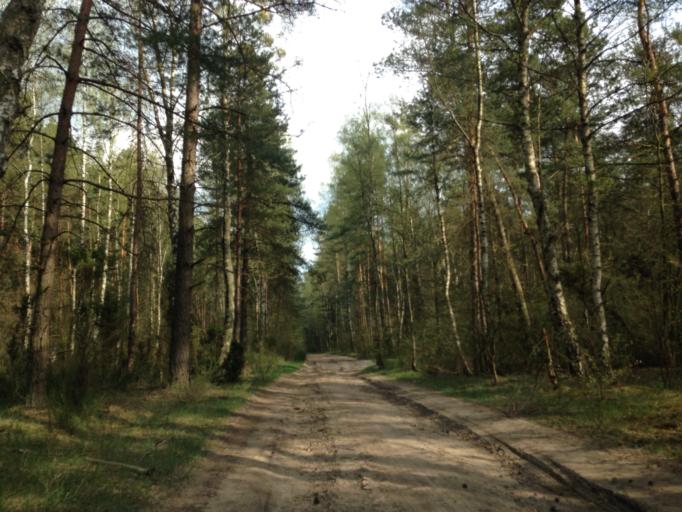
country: PL
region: Kujawsko-Pomorskie
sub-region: Powiat brodnicki
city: Gorzno
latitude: 53.1192
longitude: 19.7161
